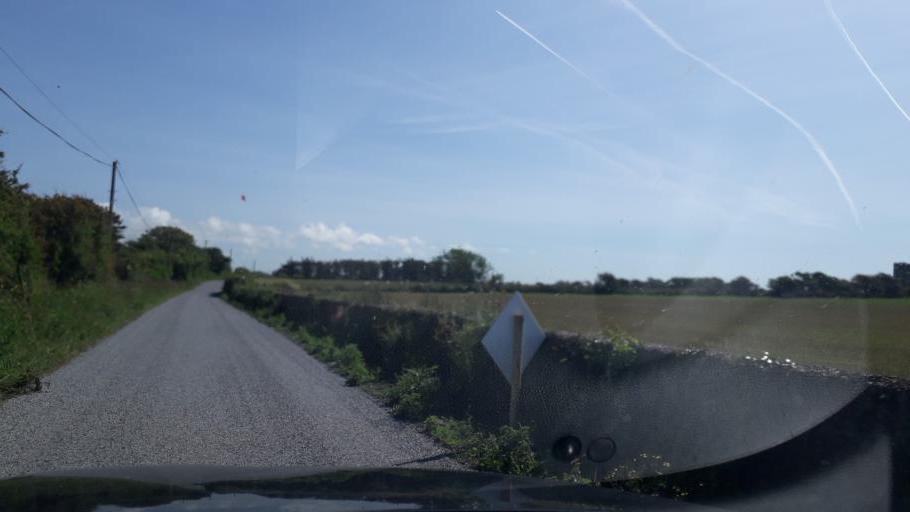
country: IE
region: Leinster
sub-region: Loch Garman
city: Loch Garman
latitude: 52.1892
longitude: -6.5575
